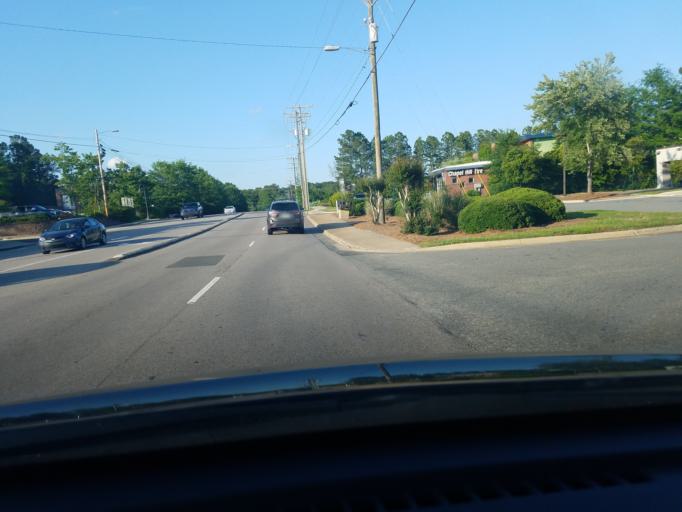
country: US
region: North Carolina
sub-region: Durham County
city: Durham
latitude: 35.9205
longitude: -78.9592
